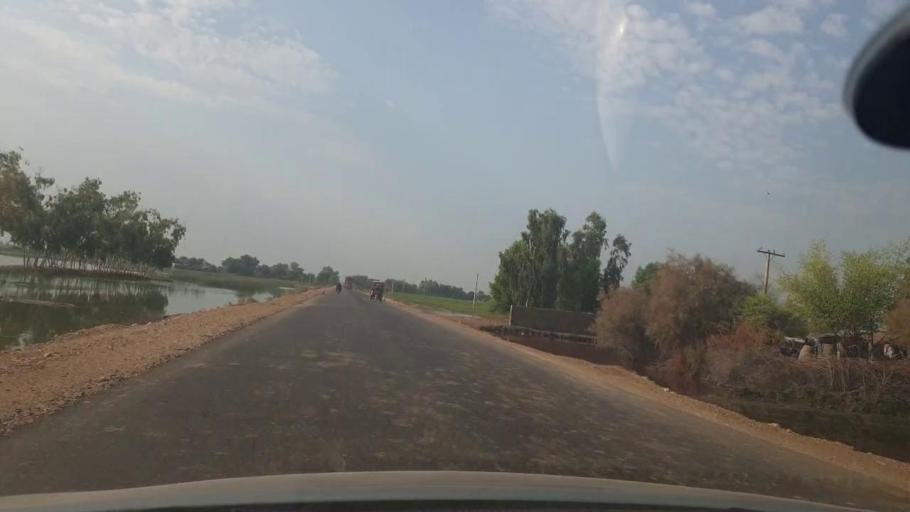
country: PK
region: Sindh
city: Jacobabad
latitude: 28.1166
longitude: 68.3272
